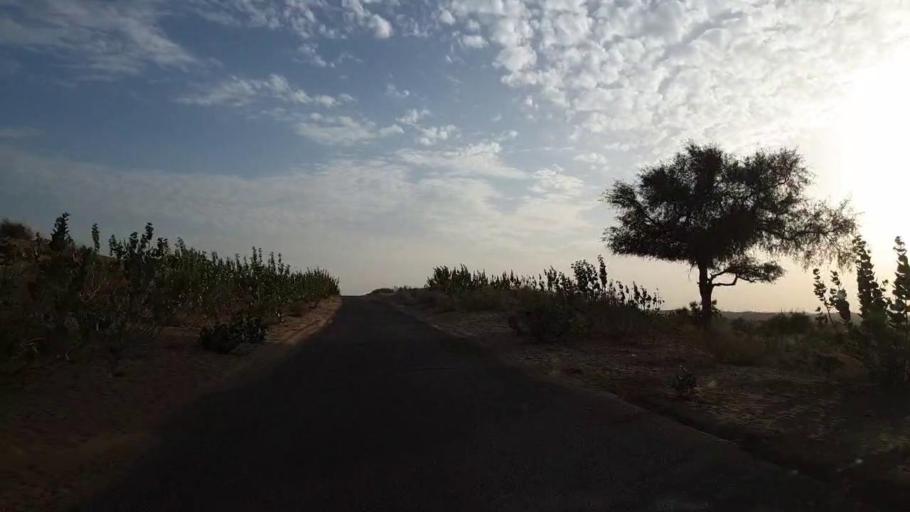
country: PK
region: Sindh
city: Umarkot
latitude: 25.1232
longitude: 70.0027
